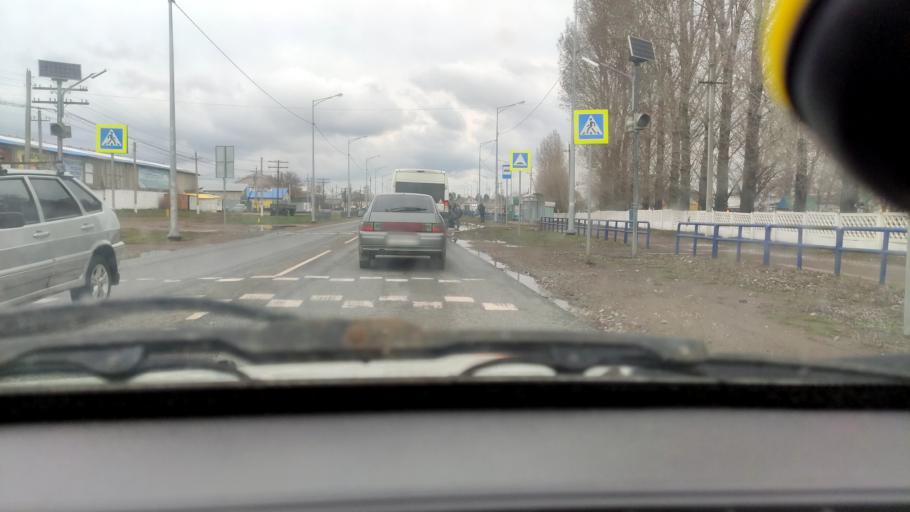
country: RU
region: Samara
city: Zhigulevsk
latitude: 53.5497
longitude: 49.5246
